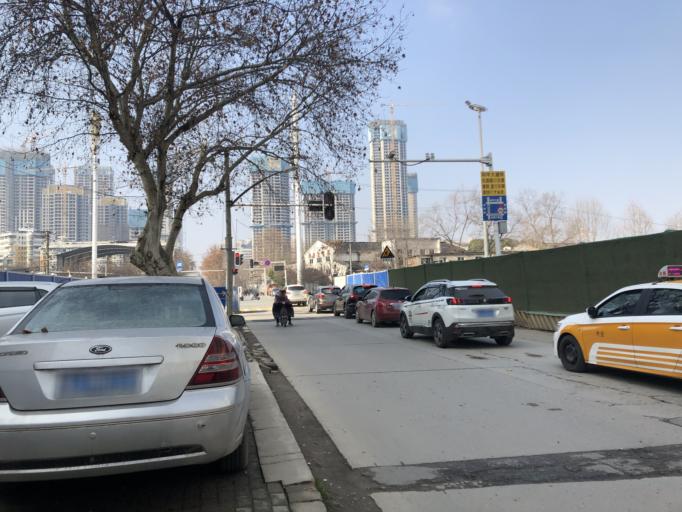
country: CN
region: Hubei
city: Jiang'an
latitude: 30.6034
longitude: 114.3494
